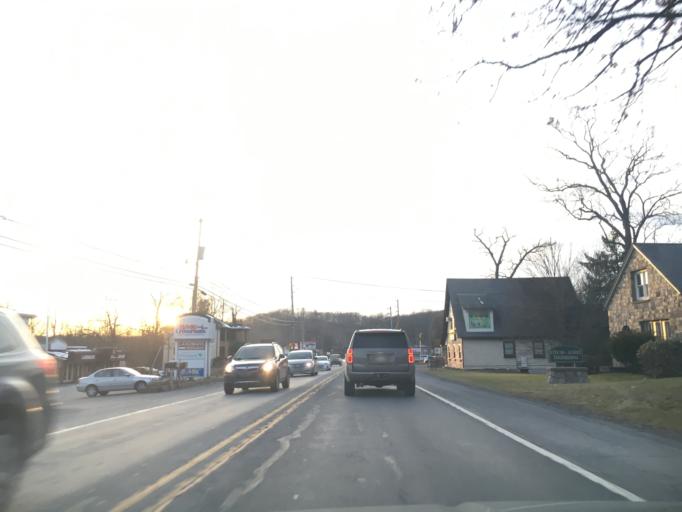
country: US
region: Pennsylvania
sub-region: Monroe County
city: East Stroudsburg
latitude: 41.0030
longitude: -75.1478
